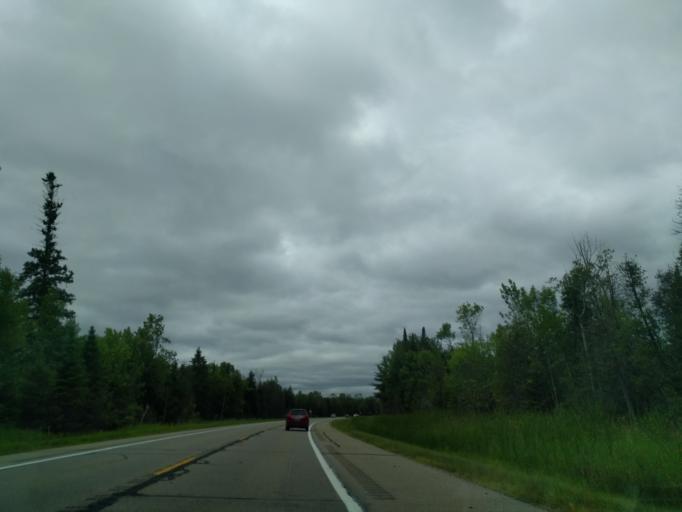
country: US
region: Michigan
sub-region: Delta County
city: Escanaba
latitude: 45.5989
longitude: -87.2266
